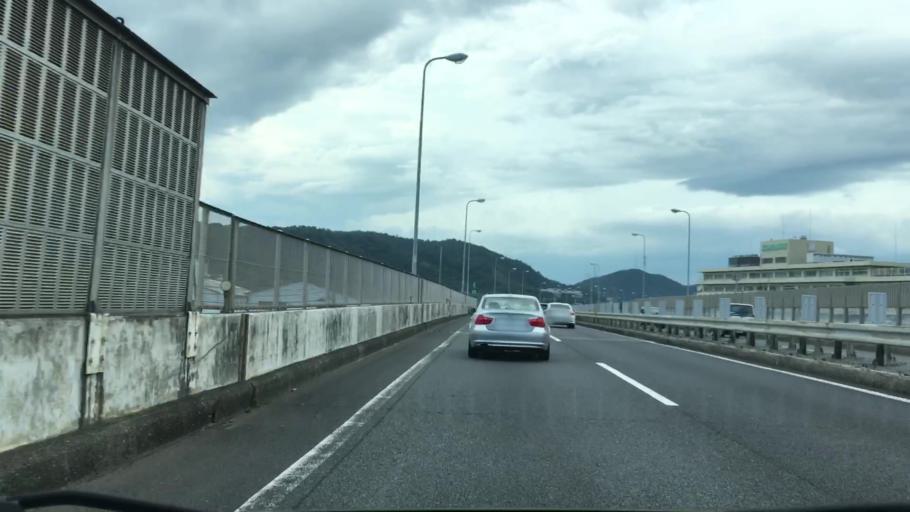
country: JP
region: Hyogo
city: Shirahamacho-usazakiminami
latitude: 34.7877
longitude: 134.7740
